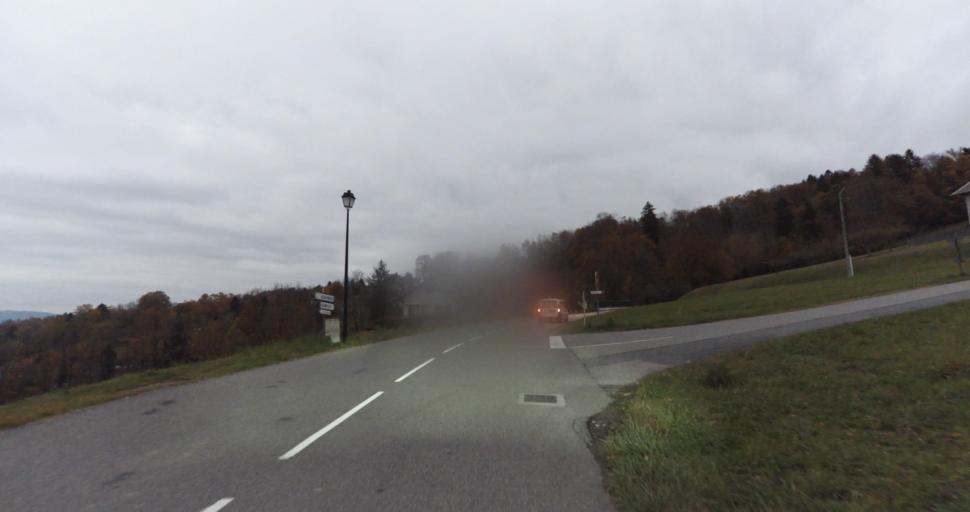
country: FR
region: Rhone-Alpes
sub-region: Departement de la Haute-Savoie
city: Alby-sur-Cheran
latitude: 45.8392
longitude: 6.0067
